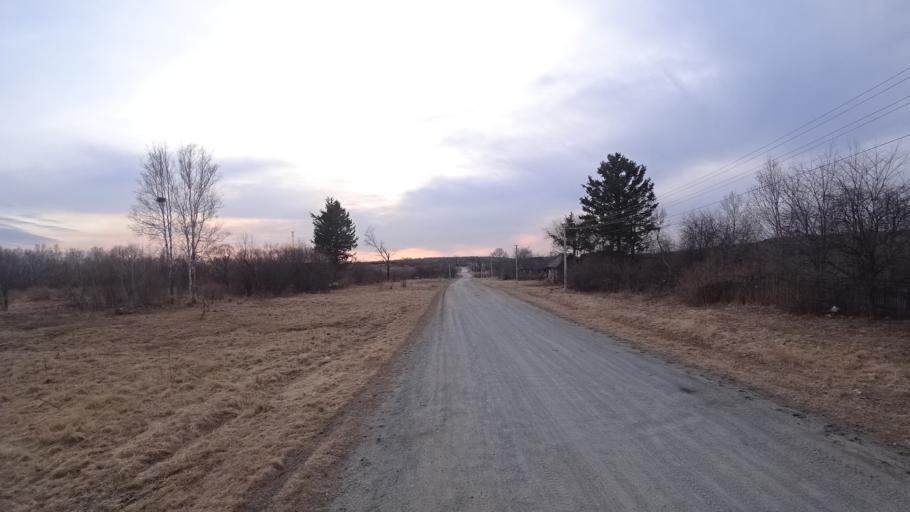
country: RU
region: Amur
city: Bureya
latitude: 50.0202
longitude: 129.7680
